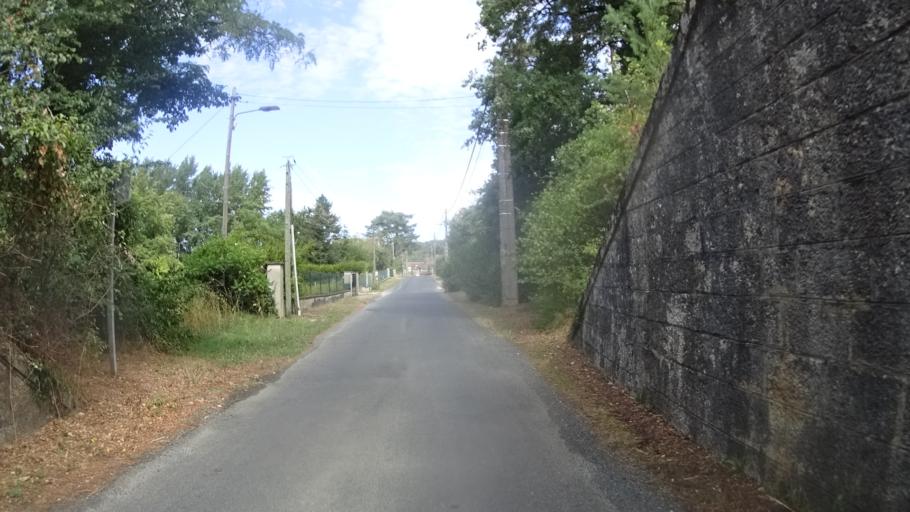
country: FR
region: Centre
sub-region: Departement du Loiret
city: Malesherbes
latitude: 48.2748
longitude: 2.4248
